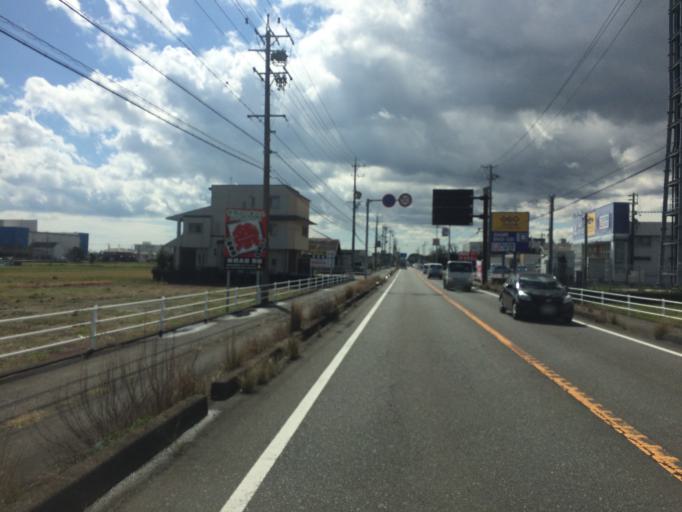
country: JP
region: Shizuoka
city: Fujieda
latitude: 34.8078
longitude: 138.2697
